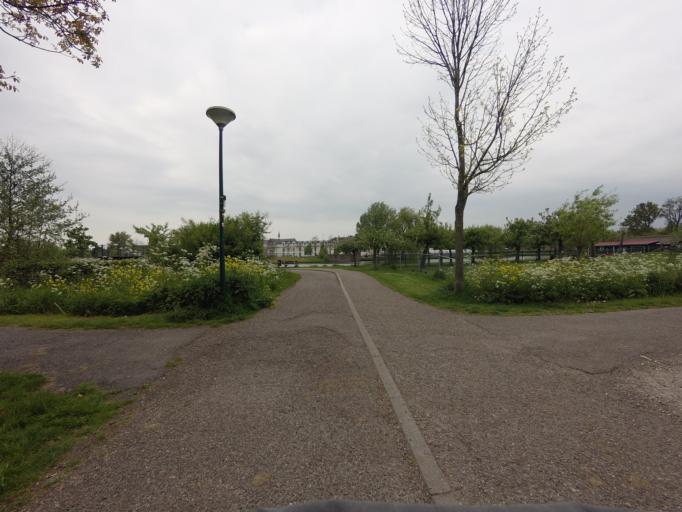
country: NL
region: Utrecht
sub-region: Gemeente Montfoort
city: Montfoort
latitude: 52.0427
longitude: 4.9507
